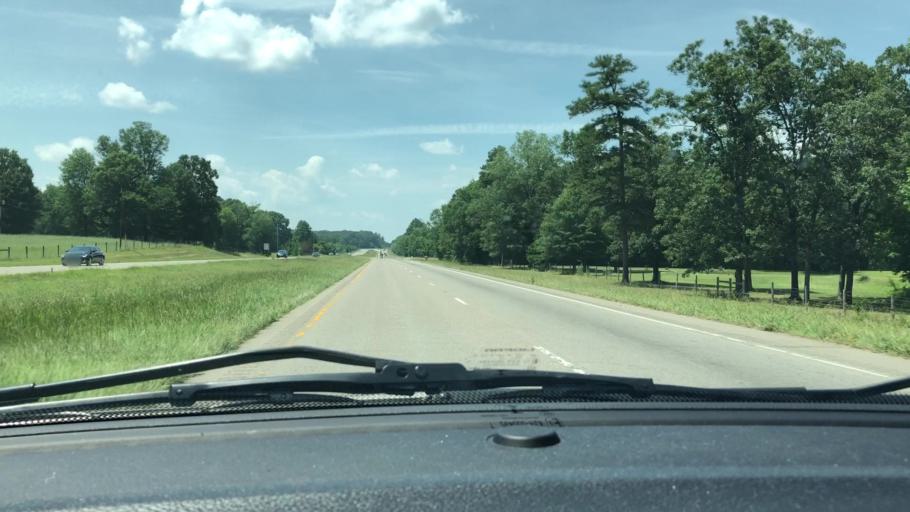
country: US
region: North Carolina
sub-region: Chatham County
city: Farmville
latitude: 35.6192
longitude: -79.3534
